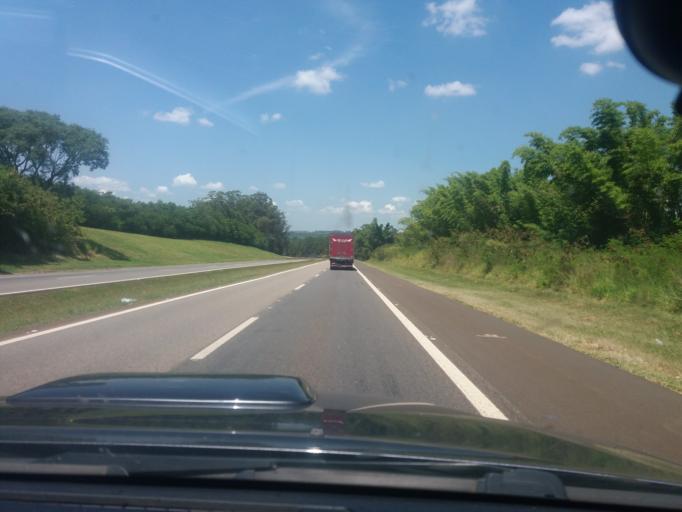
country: BR
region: Sao Paulo
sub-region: Tatui
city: Tatui
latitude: -23.3683
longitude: -47.9102
